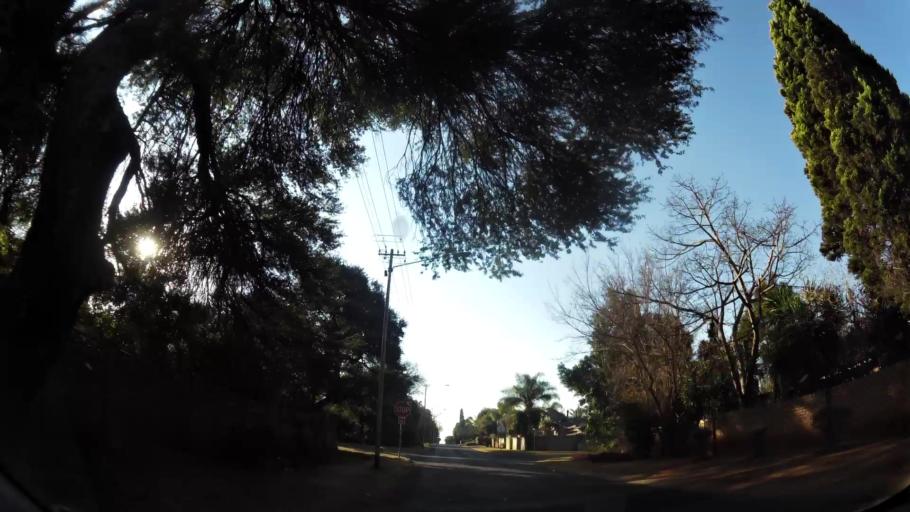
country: ZA
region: Gauteng
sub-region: City of Tshwane Metropolitan Municipality
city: Centurion
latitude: -25.8549
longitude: 28.1508
